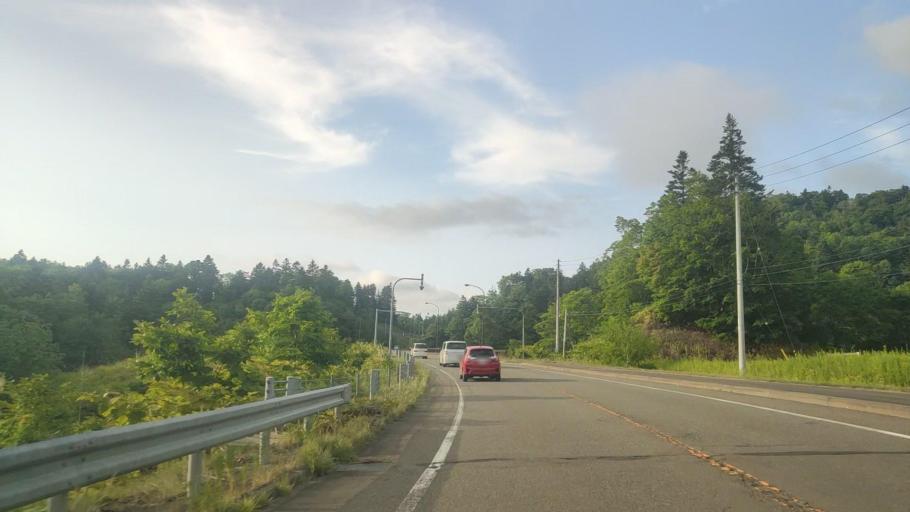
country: JP
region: Hokkaido
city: Iwamizawa
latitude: 43.0241
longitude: 141.9544
